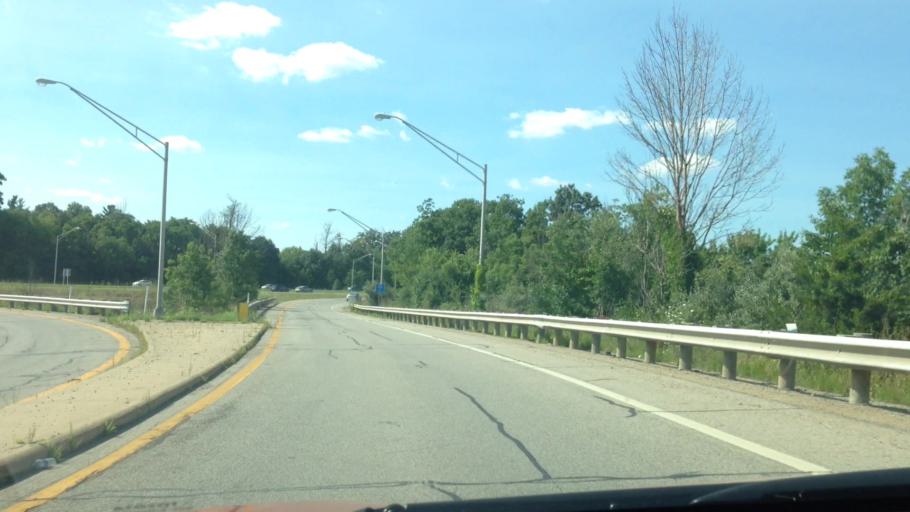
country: US
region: Ohio
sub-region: Stark County
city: Greentown
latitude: 40.9159
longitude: -81.4246
